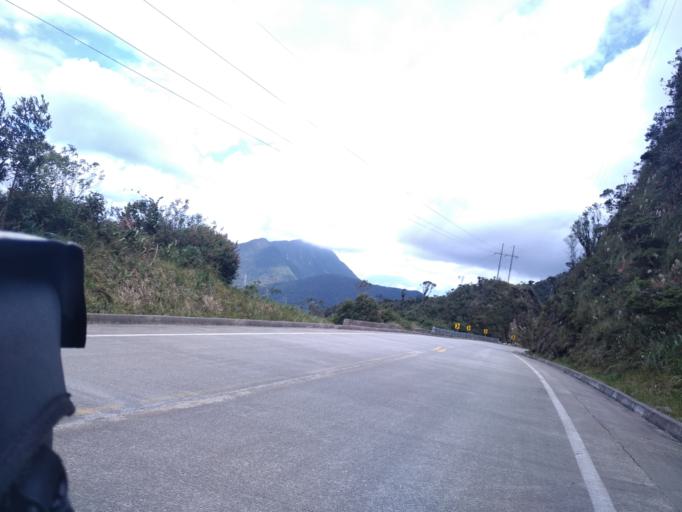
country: EC
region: Loja
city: Cariamanga
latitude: -4.4615
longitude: -79.1481
